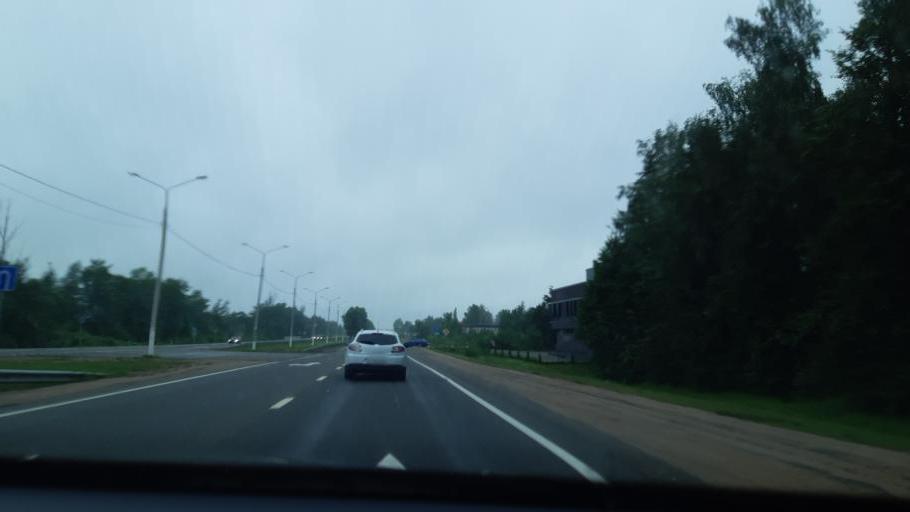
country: RU
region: Smolensk
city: Talashkino
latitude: 54.6827
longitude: 32.1390
